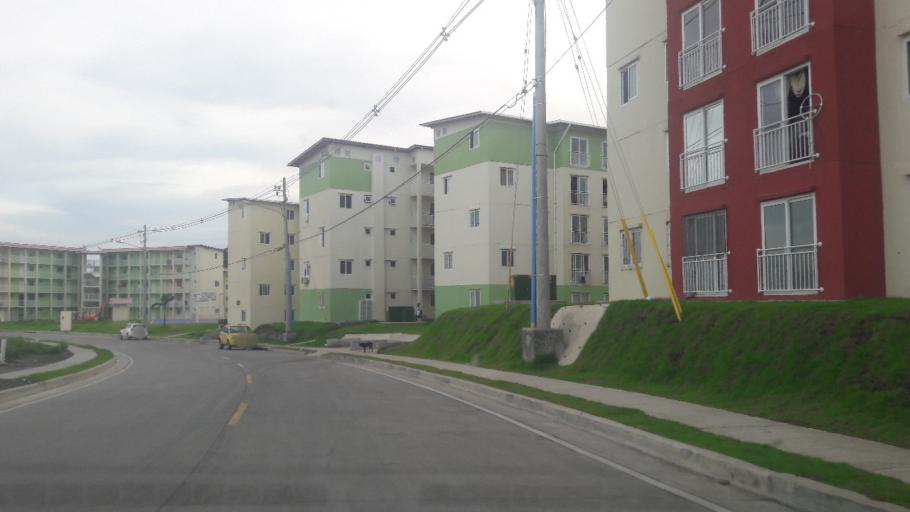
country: PA
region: Colon
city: Cativa
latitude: 9.3694
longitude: -79.8483
